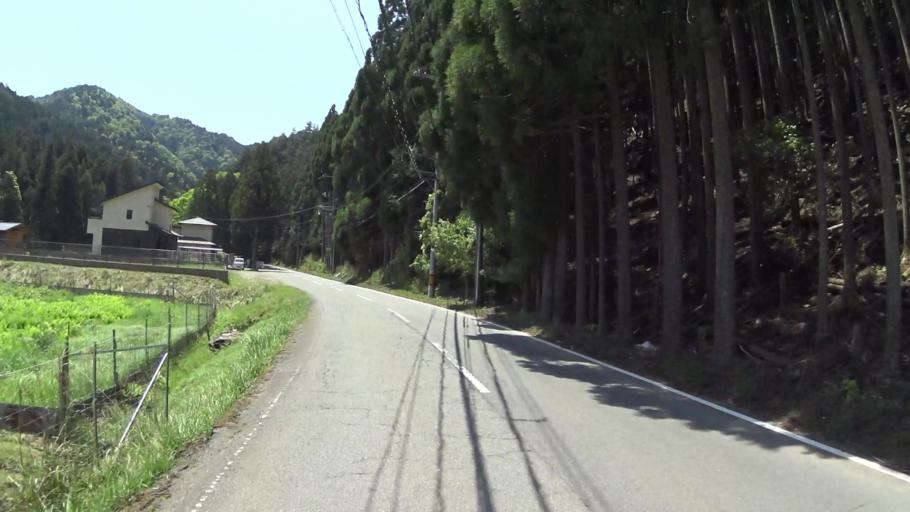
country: JP
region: Kyoto
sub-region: Kyoto-shi
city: Kamigyo-ku
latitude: 35.2030
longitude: 135.7093
